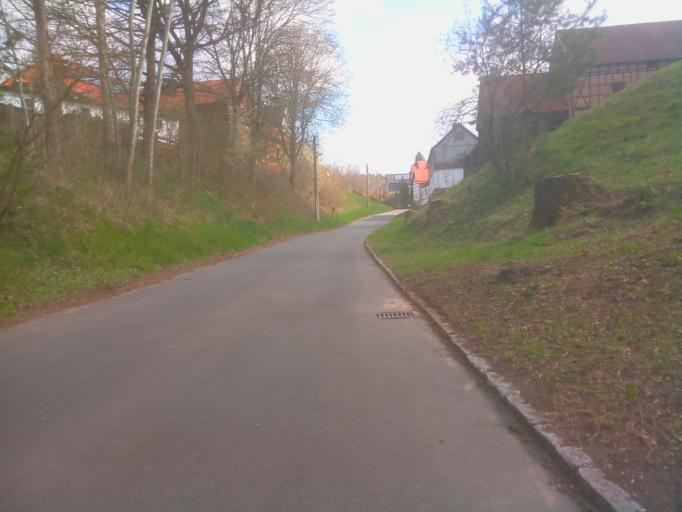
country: DE
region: Thuringia
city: Stanau
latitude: 50.7831
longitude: 11.7330
